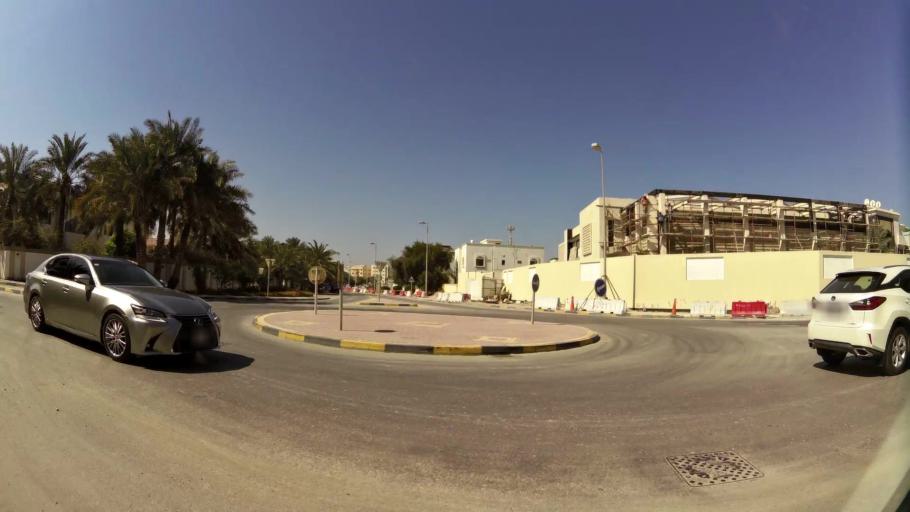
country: BH
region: Manama
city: Manama
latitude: 26.2073
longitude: 50.5812
